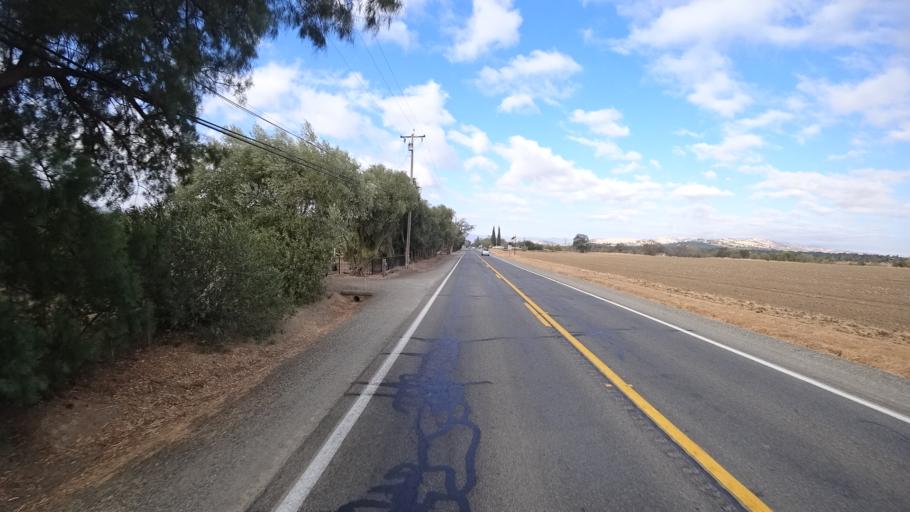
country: US
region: California
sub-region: Yolo County
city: Esparto
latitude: 38.7063
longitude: -122.0426
